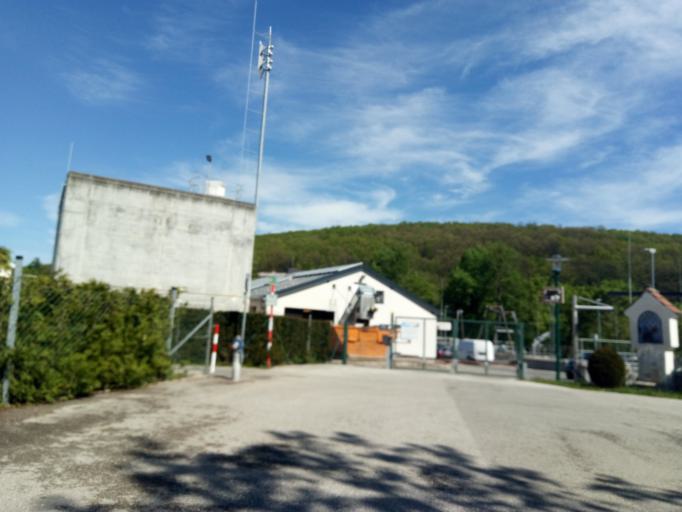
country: AT
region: Lower Austria
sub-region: Politischer Bezirk Modling
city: Kaltenleutgeben
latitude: 48.1351
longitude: 16.2107
